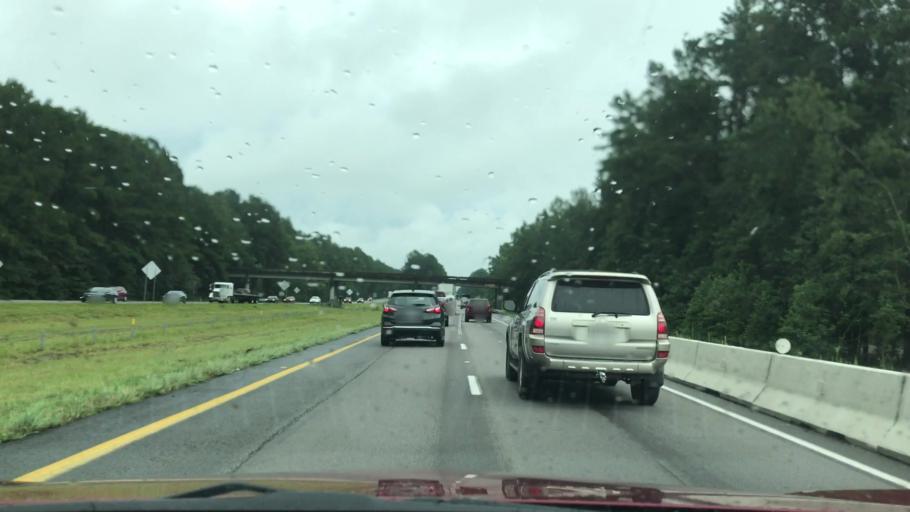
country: US
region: South Carolina
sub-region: Dorchester County
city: Ridgeville
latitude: 33.1128
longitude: -80.2633
